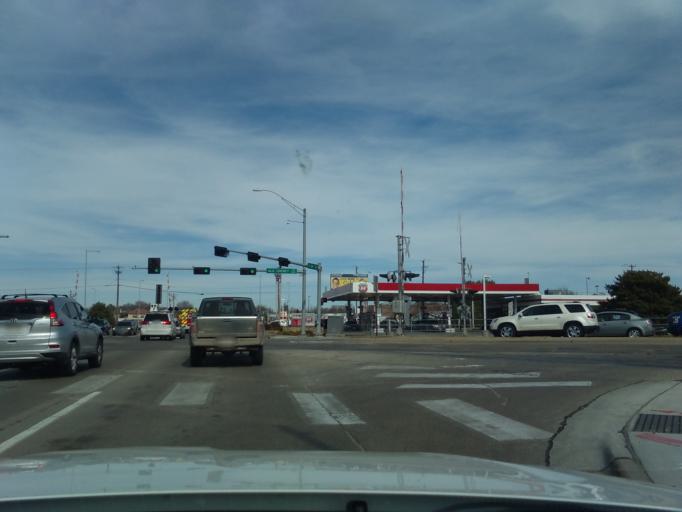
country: US
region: Nebraska
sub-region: Lancaster County
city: Lincoln
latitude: 40.7542
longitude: -96.6443
